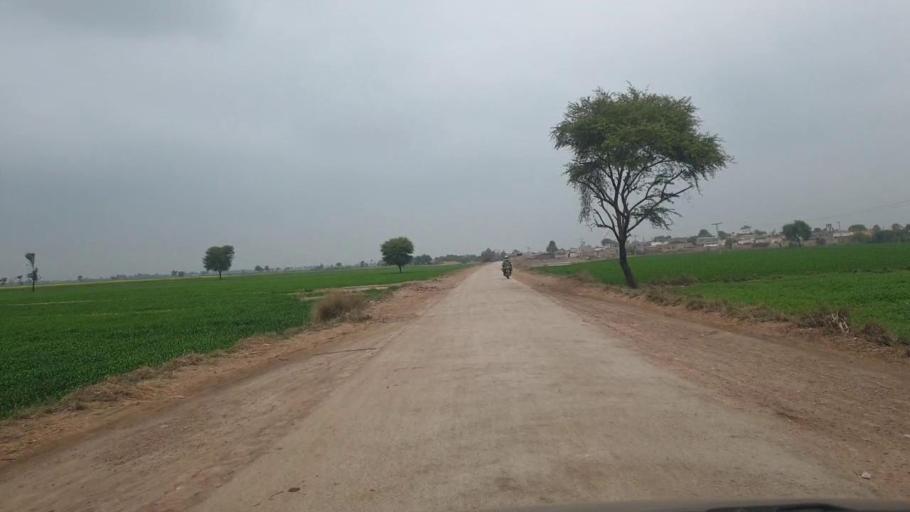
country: PK
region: Sindh
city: Shahdadpur
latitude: 25.9456
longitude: 68.7245
